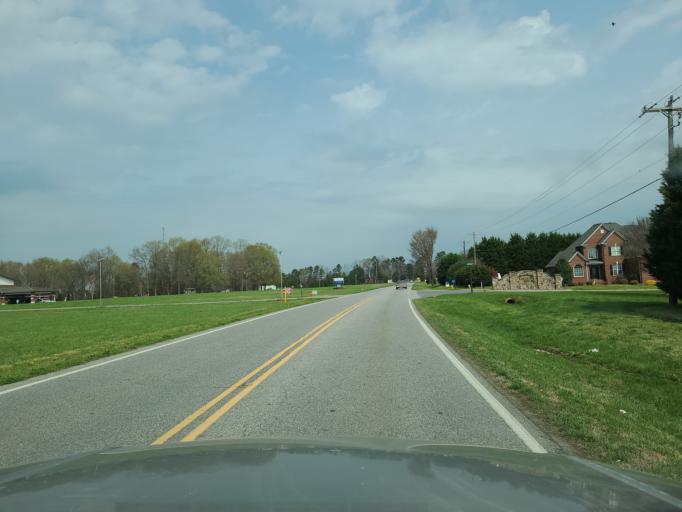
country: US
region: North Carolina
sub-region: Gaston County
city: Stanley
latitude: 35.3420
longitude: -81.0932
